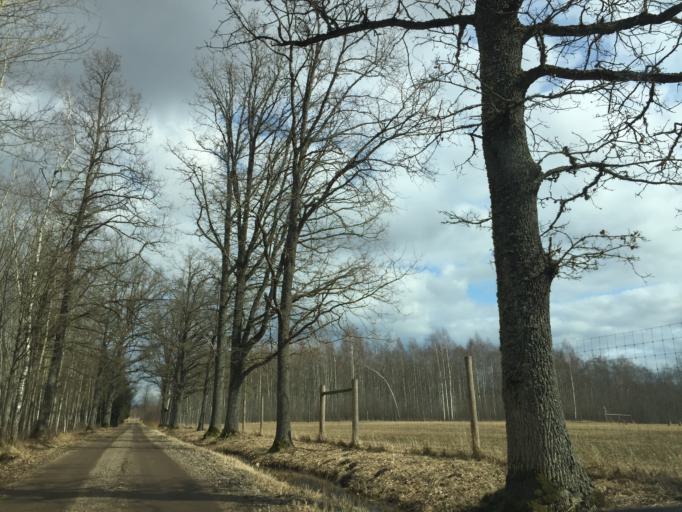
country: LV
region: Vecumnieki
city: Vecumnieki
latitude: 56.5371
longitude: 24.6949
